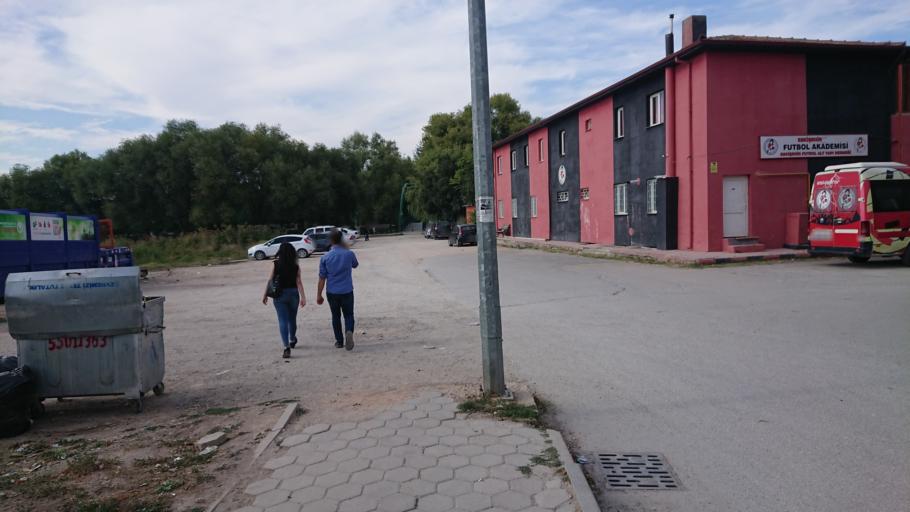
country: TR
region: Eskisehir
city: Eskisehir
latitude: 39.7681
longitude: 30.4963
